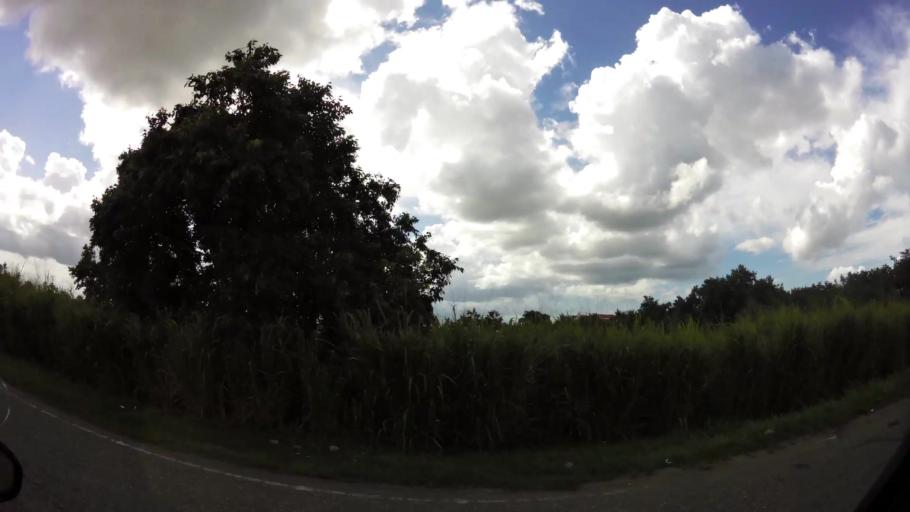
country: TT
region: Penal/Debe
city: Debe
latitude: 10.2244
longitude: -61.4417
